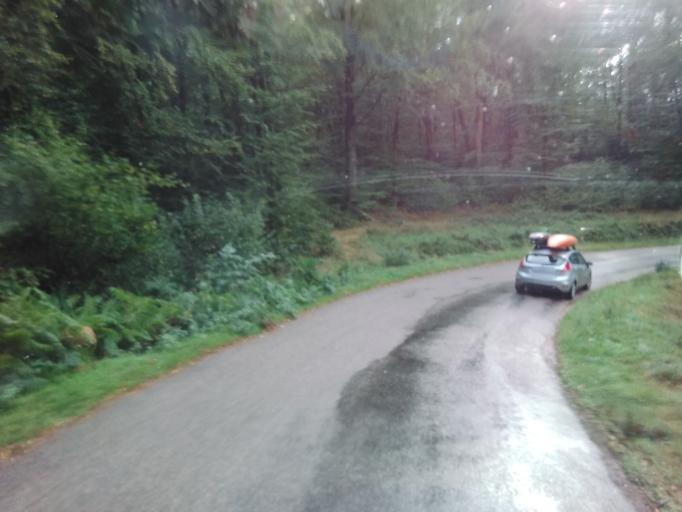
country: FR
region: Bourgogne
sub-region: Departement de la Nievre
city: Lormes
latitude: 47.2963
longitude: 3.8801
